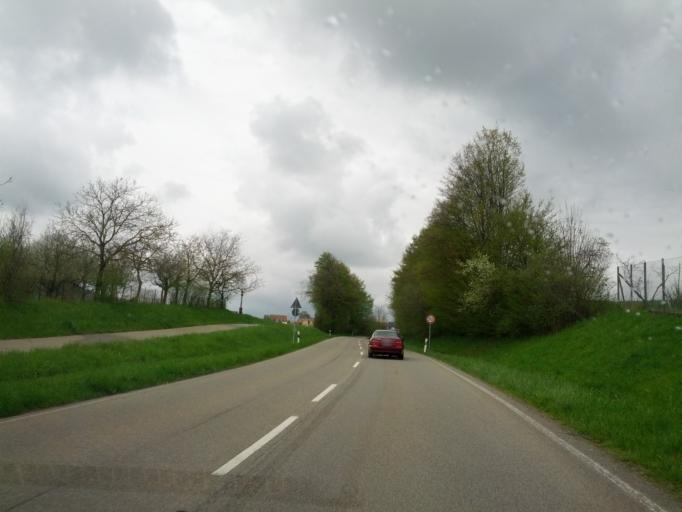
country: DE
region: Baden-Wuerttemberg
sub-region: Freiburg Region
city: Solden
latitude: 47.9353
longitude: 7.8126
